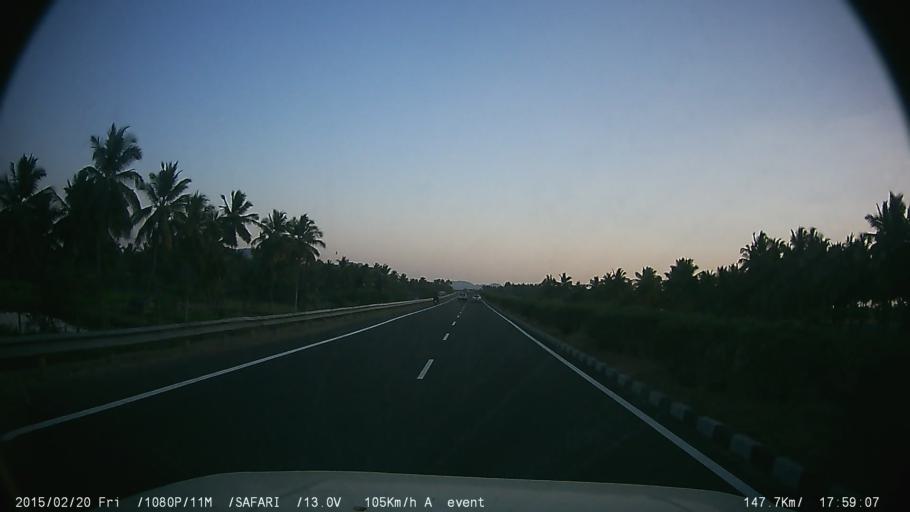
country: IN
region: Tamil Nadu
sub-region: Krishnagiri
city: Kaverippattanam
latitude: 12.4207
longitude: 78.2263
